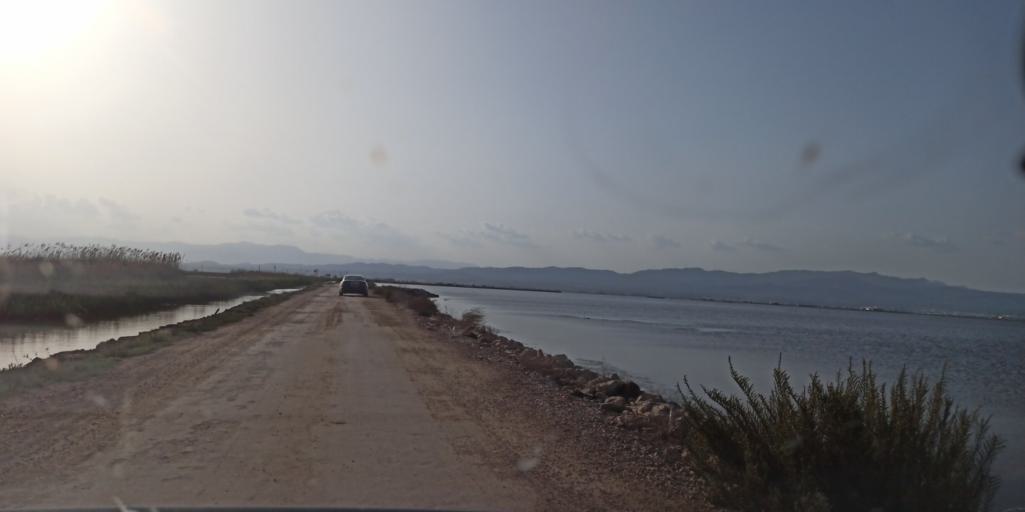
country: ES
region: Catalonia
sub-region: Provincia de Tarragona
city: Deltebre
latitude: 40.7645
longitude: 0.7487
